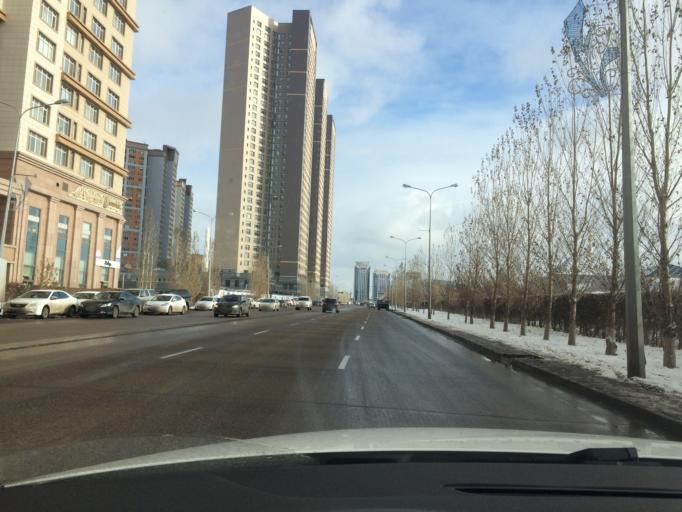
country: KZ
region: Astana Qalasy
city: Astana
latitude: 51.1265
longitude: 71.4624
